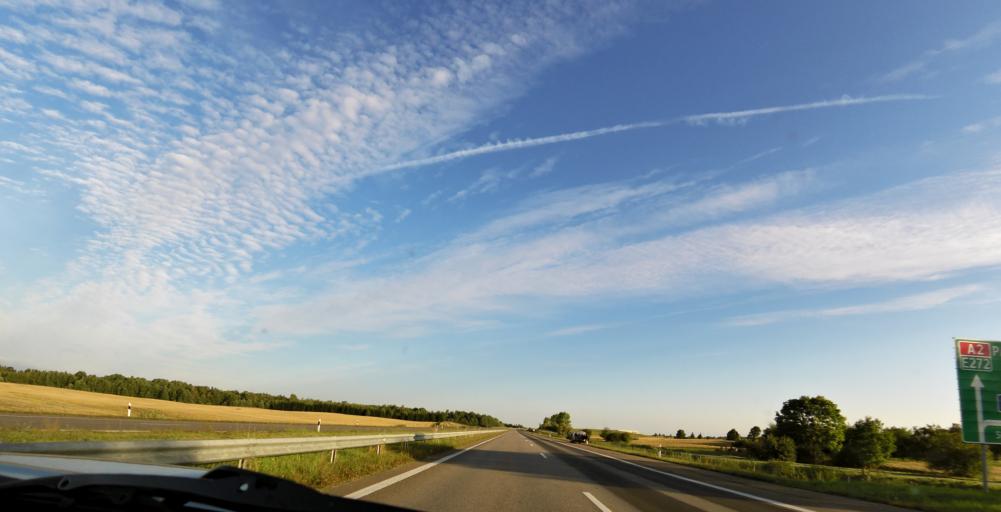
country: LT
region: Vilnius County
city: Ukmerge
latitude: 55.1688
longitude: 24.8156
